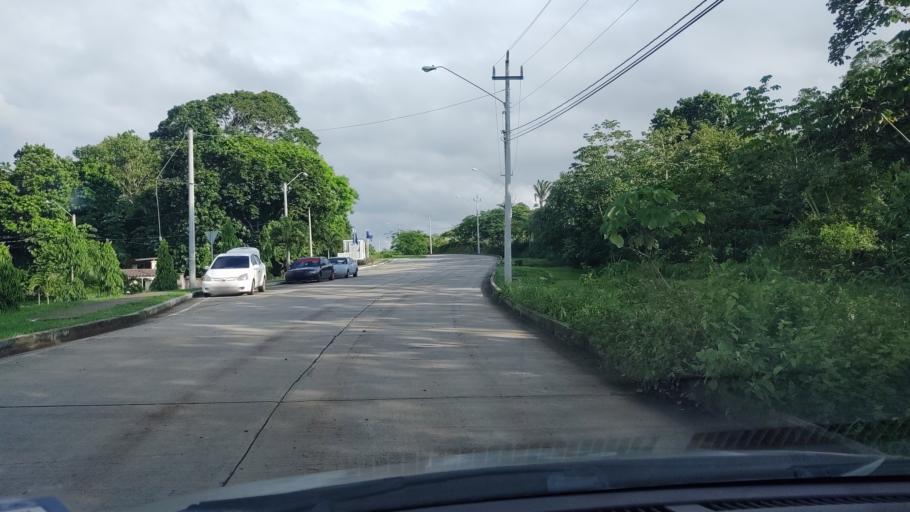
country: PA
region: Panama
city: Nuevo Arraijan
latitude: 8.9260
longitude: -79.7618
